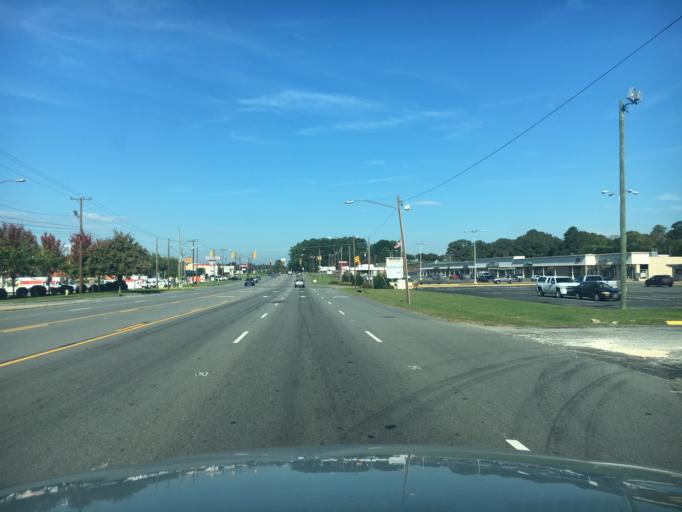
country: US
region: North Carolina
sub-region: Catawba County
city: Hickory
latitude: 35.7174
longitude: -81.3407
